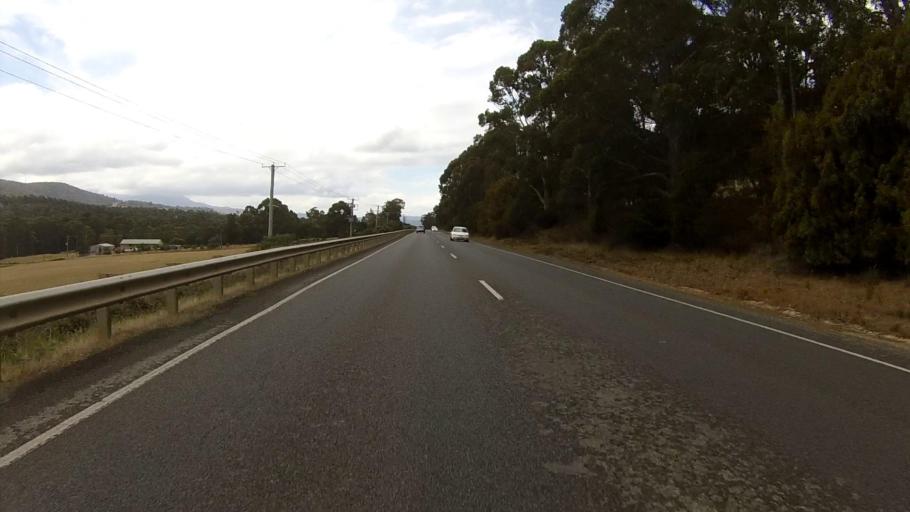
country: AU
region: Tasmania
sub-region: Kingborough
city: Kettering
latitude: -43.0835
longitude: 147.2532
